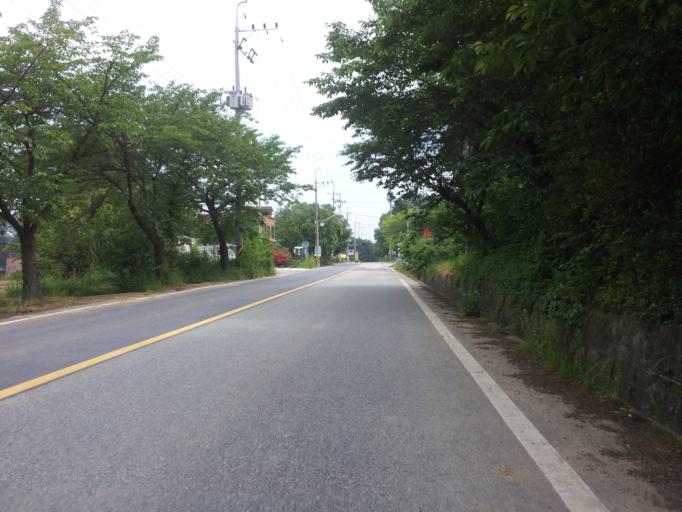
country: KR
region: Chungcheongbuk-do
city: Okcheon
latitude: 36.3650
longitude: 127.5026
